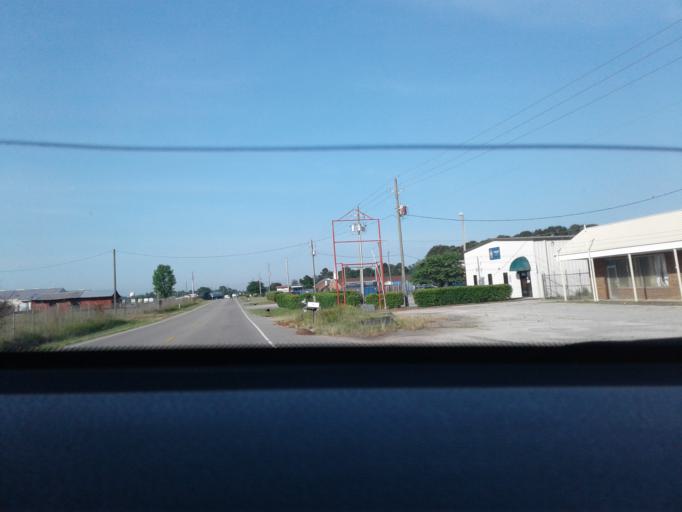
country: US
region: North Carolina
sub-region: Harnett County
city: Dunn
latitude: 35.3327
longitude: -78.5926
